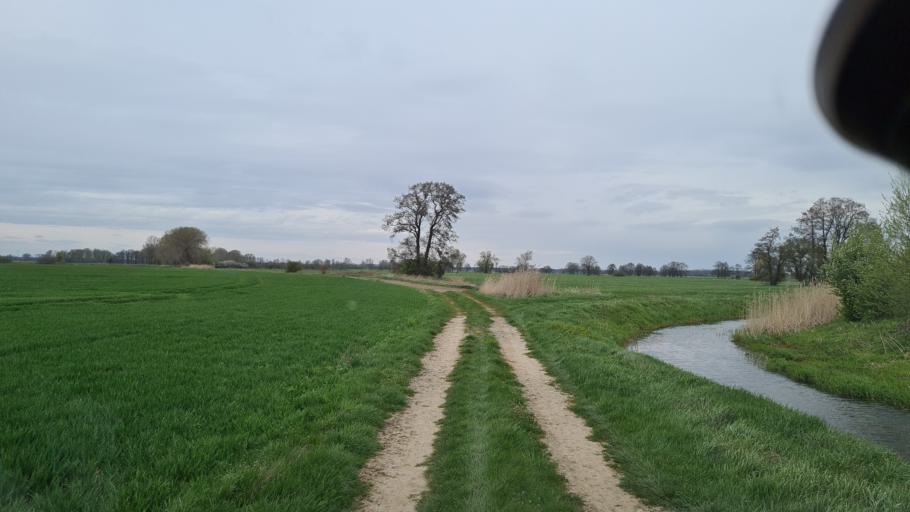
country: DE
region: Brandenburg
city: Doberlug-Kirchhain
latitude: 51.6629
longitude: 13.5659
